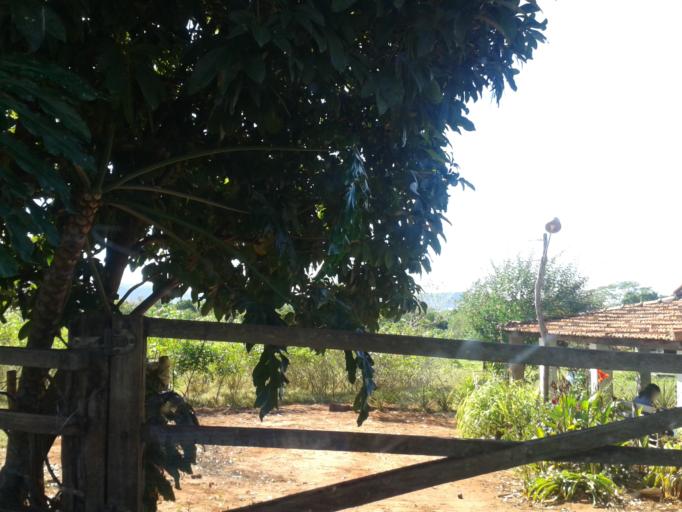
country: BR
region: Minas Gerais
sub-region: Santa Vitoria
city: Santa Vitoria
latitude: -19.1760
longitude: -50.0169
